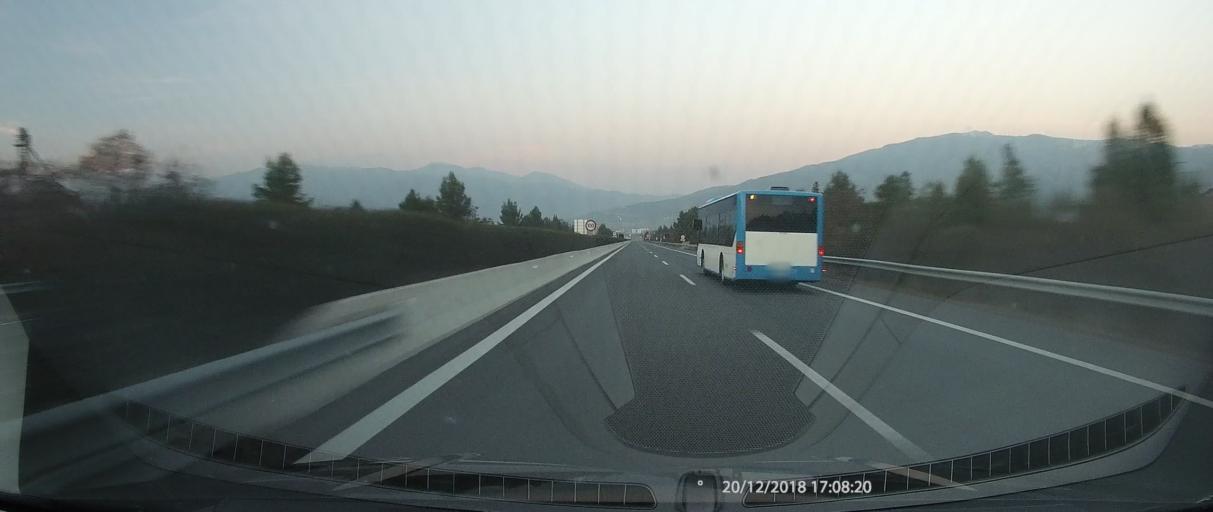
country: GR
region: Thessaly
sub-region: Nomos Larisis
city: Makrychori
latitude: 39.7961
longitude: 22.4981
